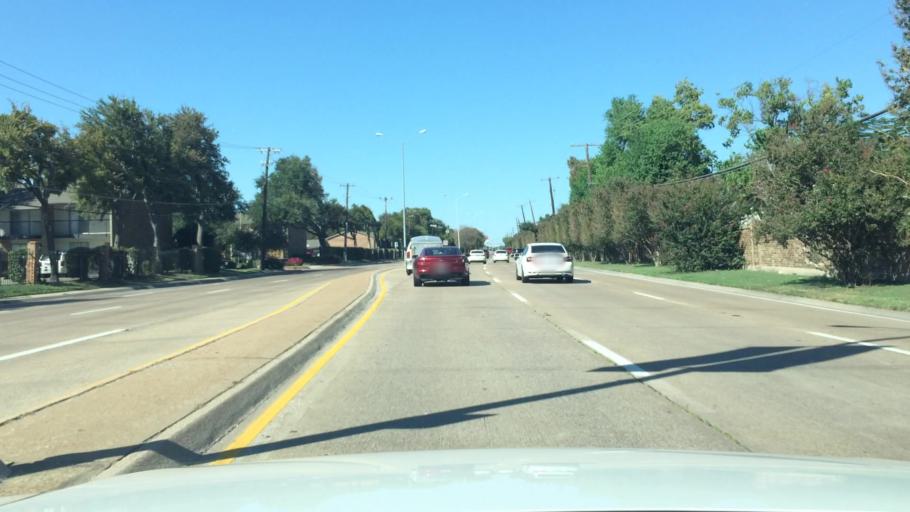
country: US
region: Texas
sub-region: Dallas County
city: Addison
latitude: 32.9563
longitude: -96.8045
